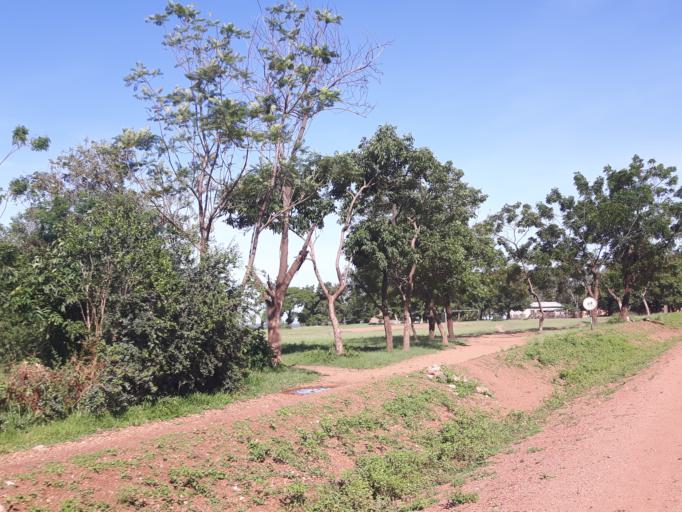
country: TZ
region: Mara
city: Issenye
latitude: -2.0249
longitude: 34.4517
